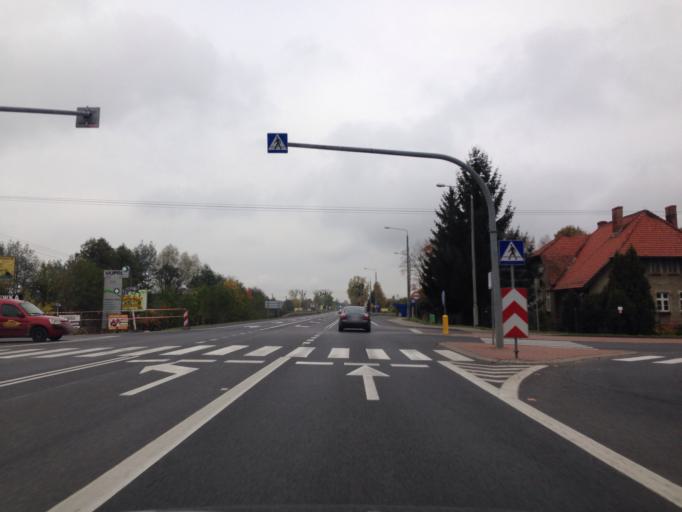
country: PL
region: Kujawsko-Pomorskie
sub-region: Powiat bydgoski
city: Osielsko
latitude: 53.2069
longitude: 18.1004
